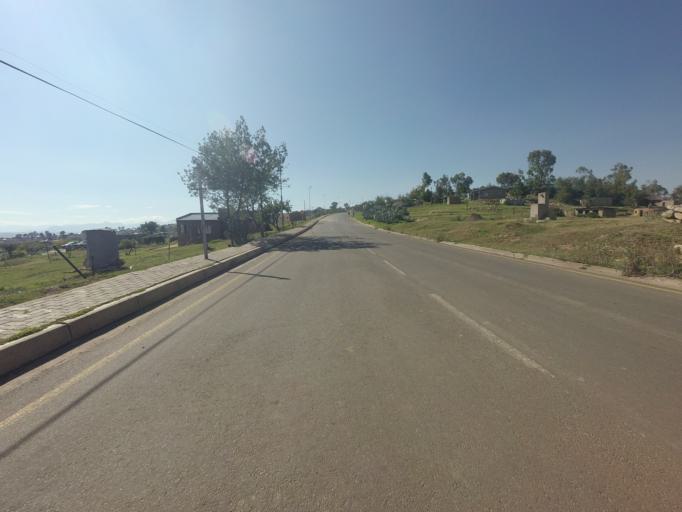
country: LS
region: Berea
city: Teyateyaneng
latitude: -29.1306
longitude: 27.7457
